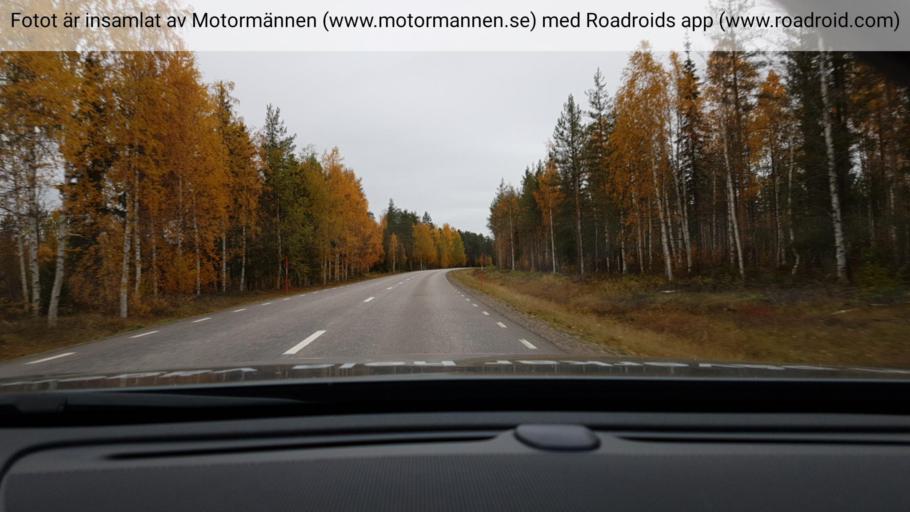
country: SE
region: Norrbotten
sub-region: Overkalix Kommun
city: OEverkalix
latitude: 66.5041
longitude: 22.7656
